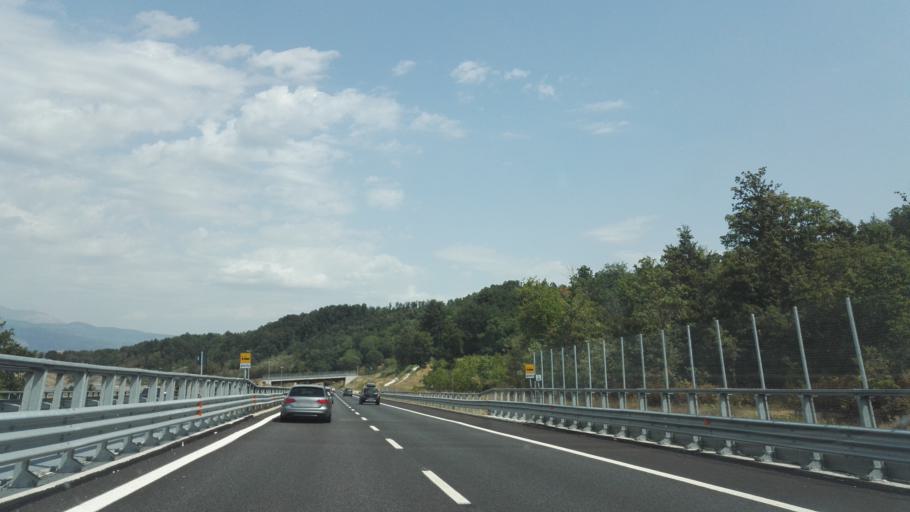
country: IT
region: Calabria
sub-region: Provincia di Cosenza
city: Laino Castello-Nuovo Centro
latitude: 39.9142
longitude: 15.9649
